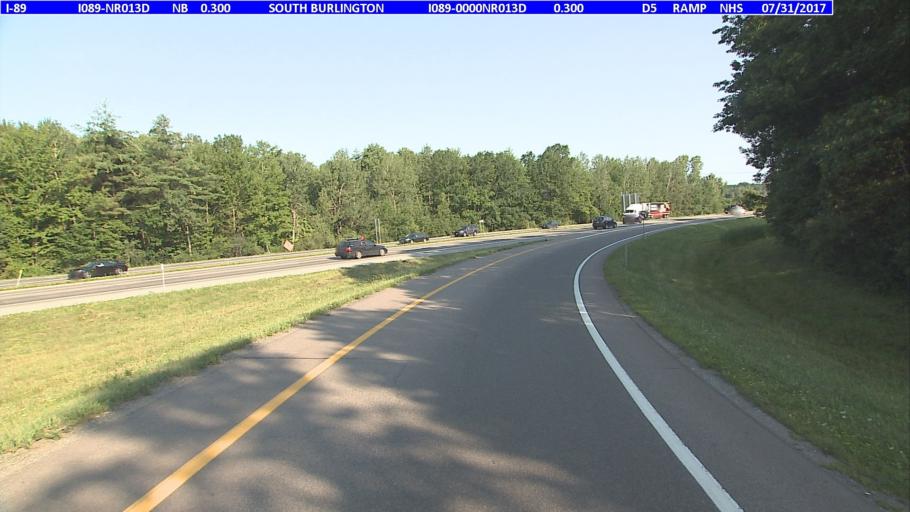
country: US
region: Vermont
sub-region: Chittenden County
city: South Burlington
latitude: 44.4547
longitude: -73.1833
